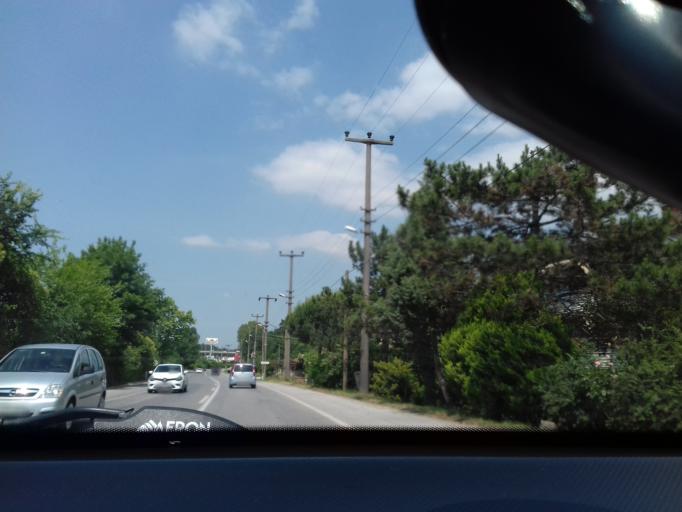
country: TR
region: Sakarya
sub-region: Merkez
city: Sapanca
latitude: 40.7000
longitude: 30.3076
